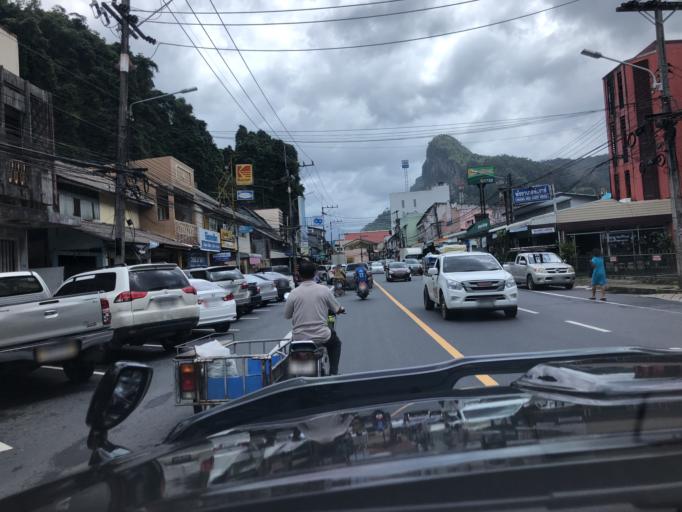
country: TH
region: Phangnga
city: Phang Nga
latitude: 8.4657
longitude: 98.5311
